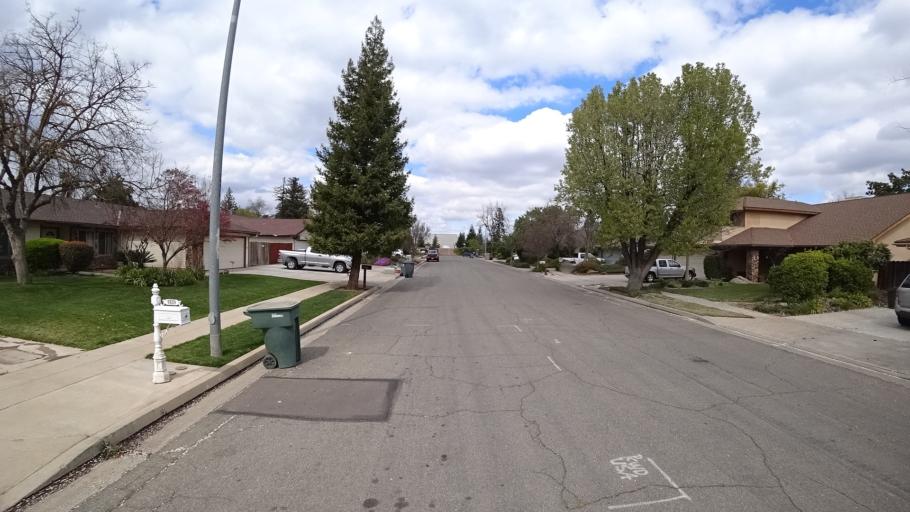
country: US
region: California
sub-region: Fresno County
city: Fresno
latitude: 36.8343
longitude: -119.8033
